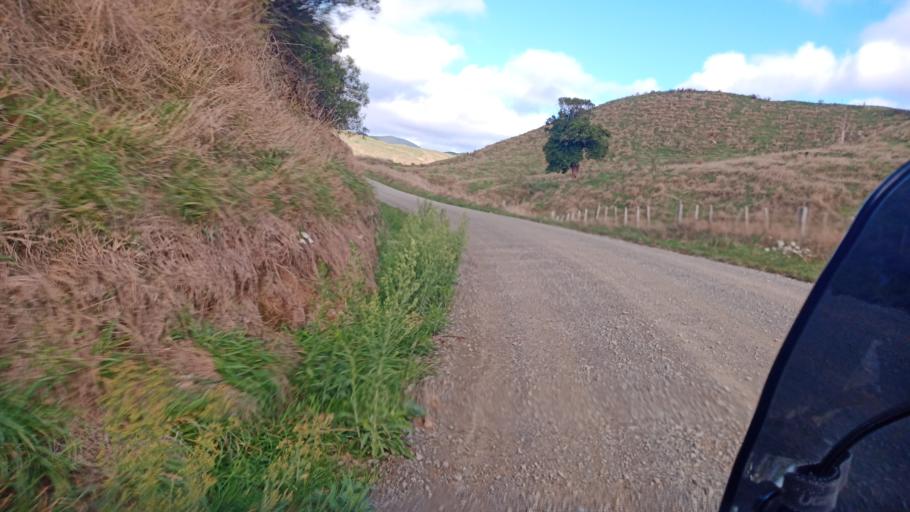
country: NZ
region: Bay of Plenty
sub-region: Opotiki District
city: Opotiki
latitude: -38.4541
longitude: 177.3946
